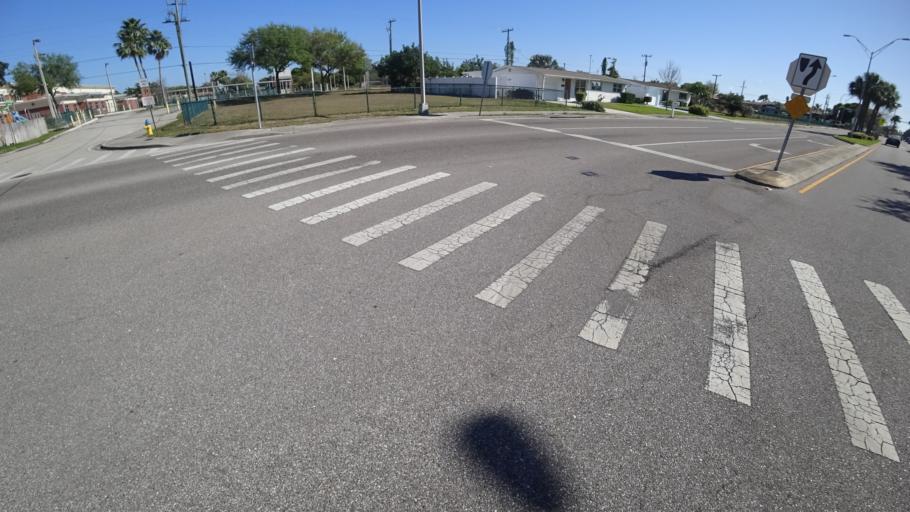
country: US
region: Florida
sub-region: Manatee County
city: Bayshore Gardens
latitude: 27.4311
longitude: -82.5895
